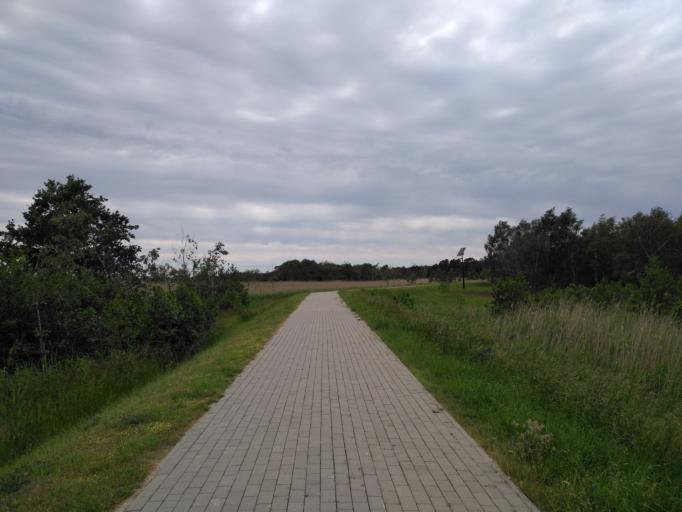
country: PL
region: West Pomeranian Voivodeship
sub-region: Powiat kolobrzeski
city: Grzybowo
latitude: 54.1518
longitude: 15.3925
